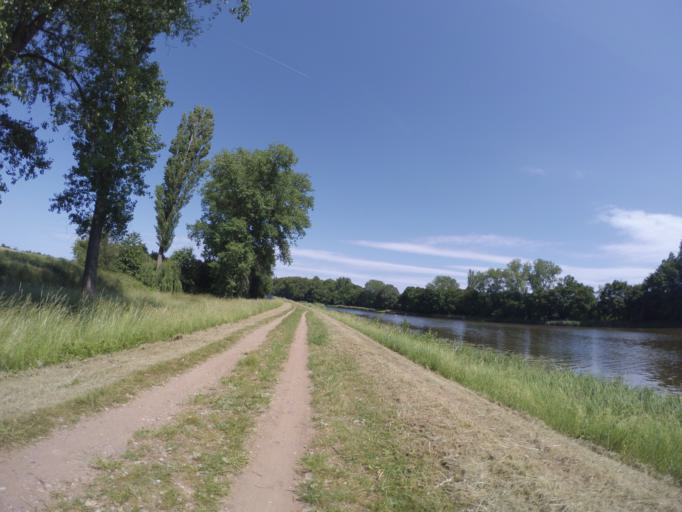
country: CZ
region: Central Bohemia
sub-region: Okres Nymburk
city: Sadska
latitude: 50.1694
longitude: 14.9967
